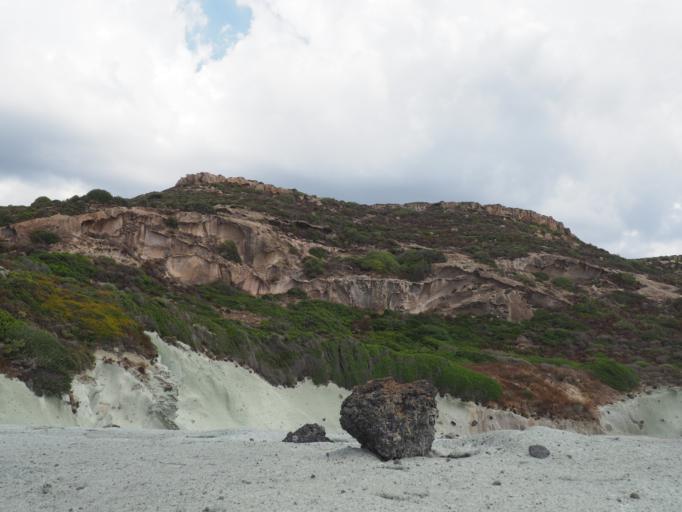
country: IT
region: Sardinia
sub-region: Provincia di Oristano
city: Bosa
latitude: 40.2941
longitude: 8.4707
